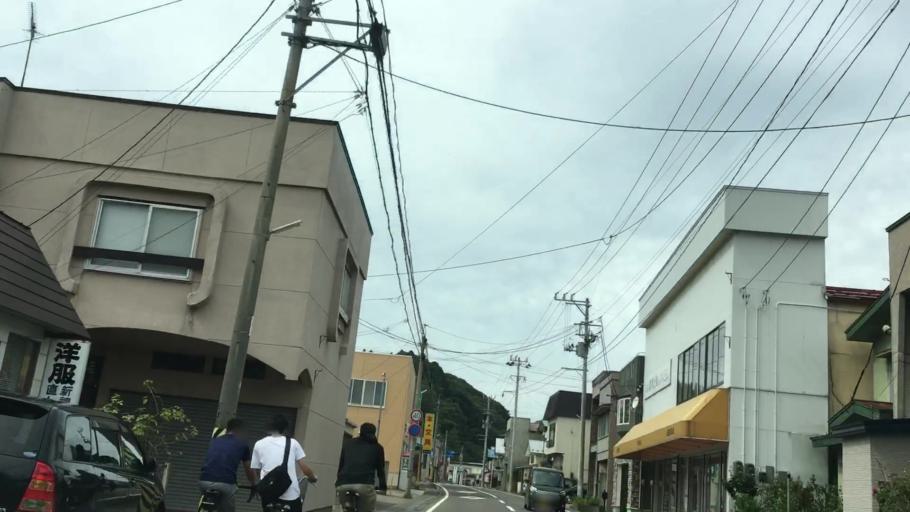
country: JP
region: Aomori
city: Shimokizukuri
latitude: 40.7781
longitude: 140.2156
